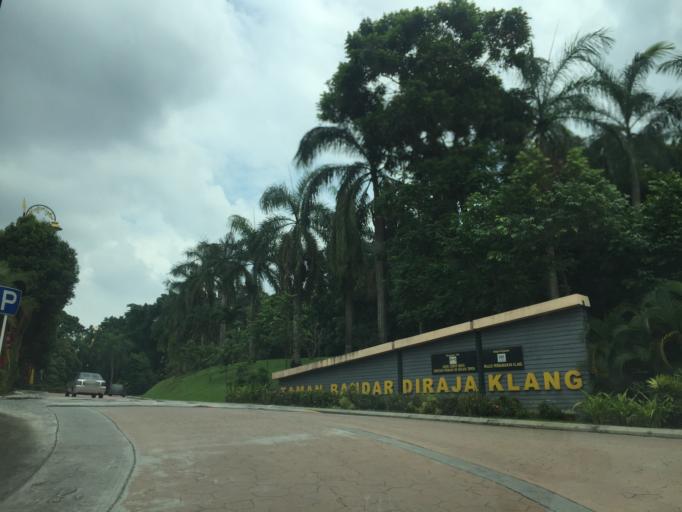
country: MY
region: Selangor
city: Klang
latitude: 3.0360
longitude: 101.4446
